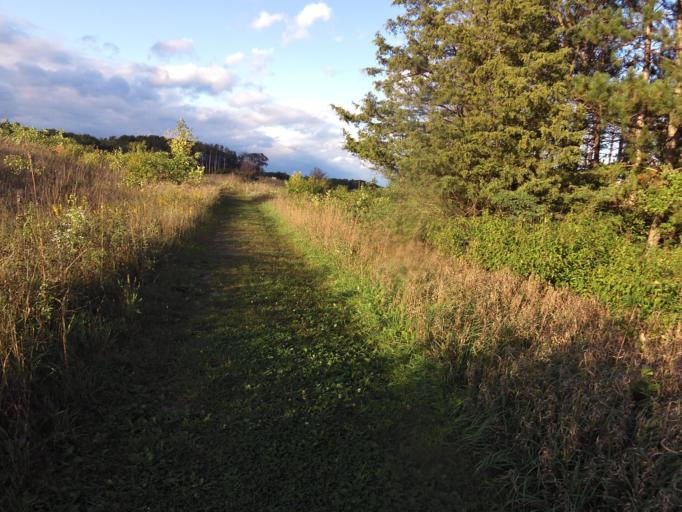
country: US
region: Minnesota
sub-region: Washington County
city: Lake Saint Croix Beach
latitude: 44.9358
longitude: -92.7868
